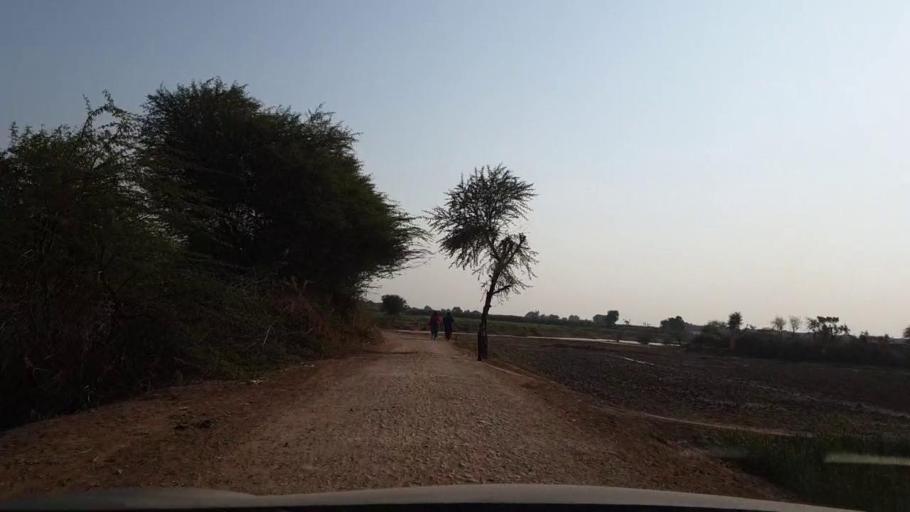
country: PK
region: Sindh
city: Tando Allahyar
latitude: 25.5835
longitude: 68.7622
